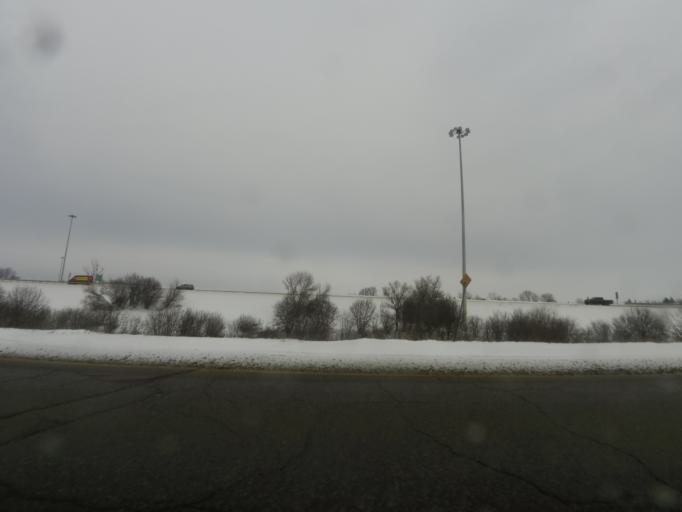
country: CA
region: Ontario
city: Ottawa
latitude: 45.4220
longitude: -75.6168
